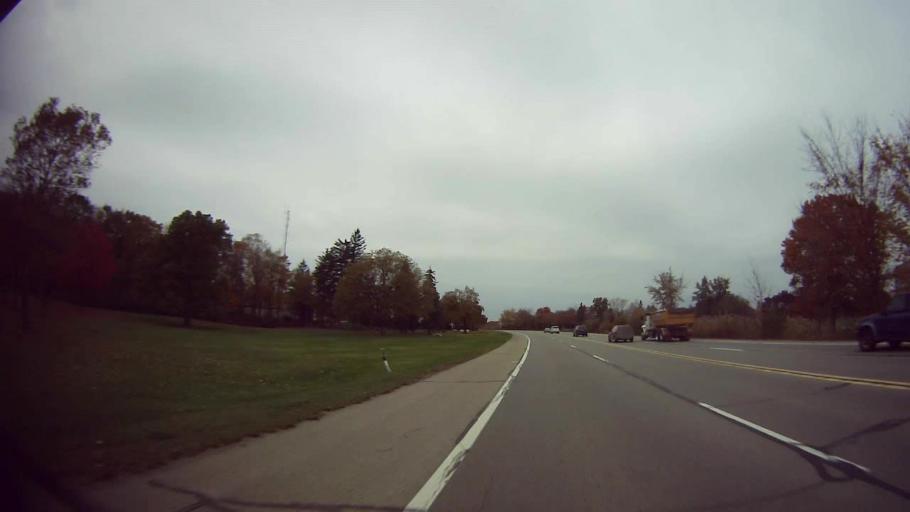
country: US
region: Michigan
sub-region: Oakland County
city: Pontiac
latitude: 42.6539
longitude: -83.3286
